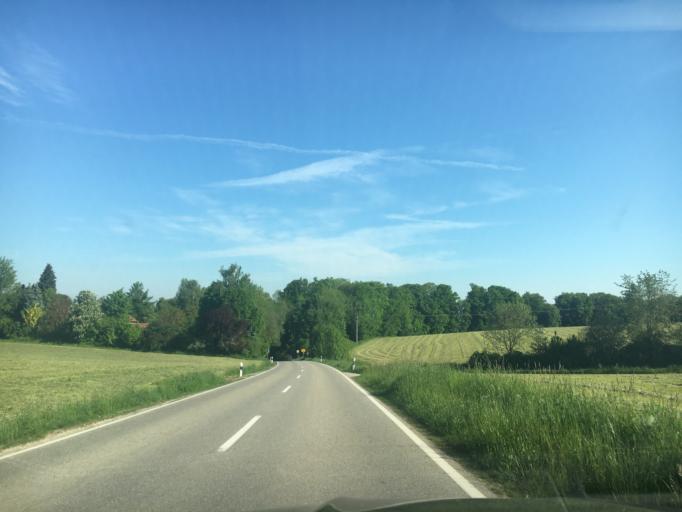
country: DE
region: Bavaria
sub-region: Upper Bavaria
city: Garching an der Alz
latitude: 48.1218
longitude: 12.5936
